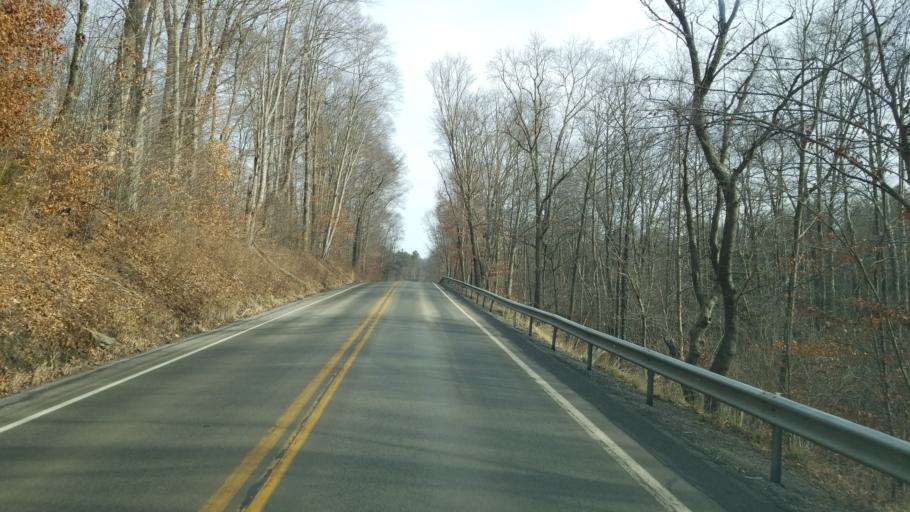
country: US
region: Pennsylvania
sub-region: Indiana County
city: Johnsonburg
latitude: 40.8149
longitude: -78.8327
